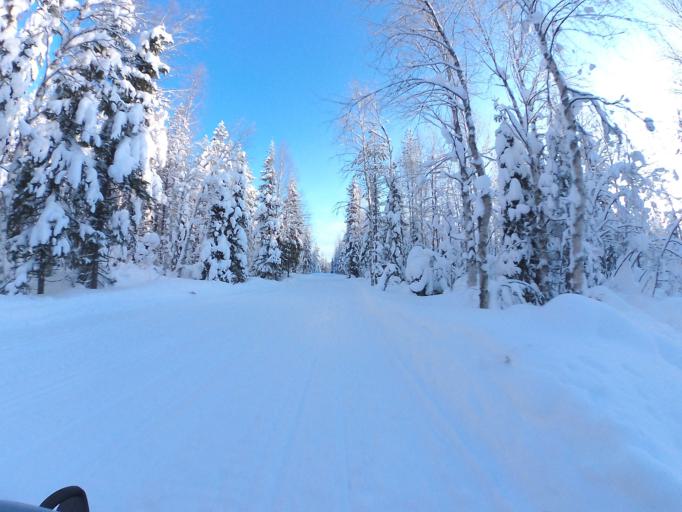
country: FI
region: Lapland
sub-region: Rovaniemi
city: Rovaniemi
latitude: 66.5965
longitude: 25.8573
